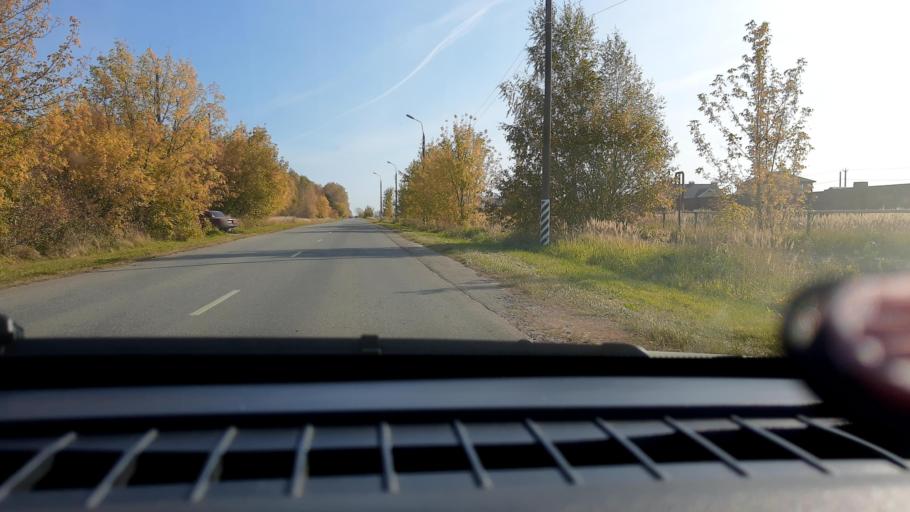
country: RU
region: Nizjnij Novgorod
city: Kstovo
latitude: 56.1552
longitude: 44.2737
